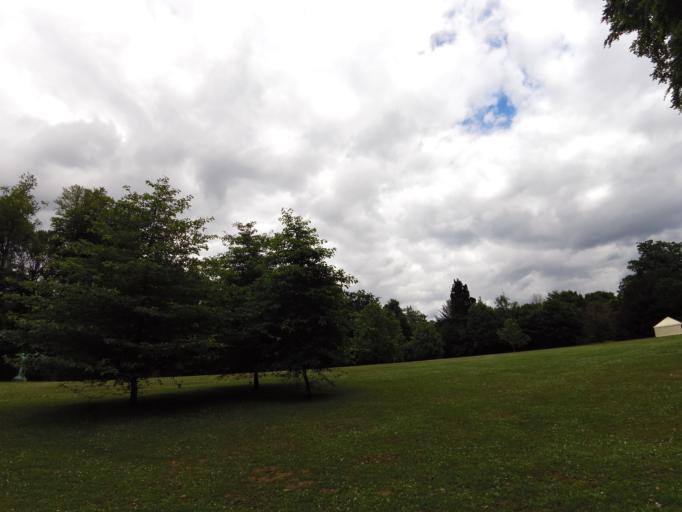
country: BE
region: Flanders
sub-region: Provincie Vlaams-Brabant
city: Meise
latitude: 50.9272
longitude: 4.3331
